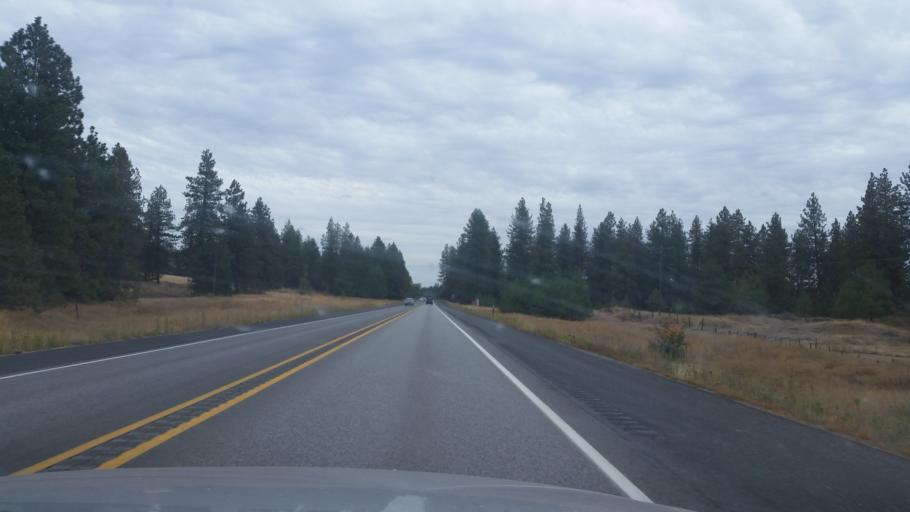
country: US
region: Washington
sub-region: Spokane County
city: Cheney
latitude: 47.5379
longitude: -117.5775
